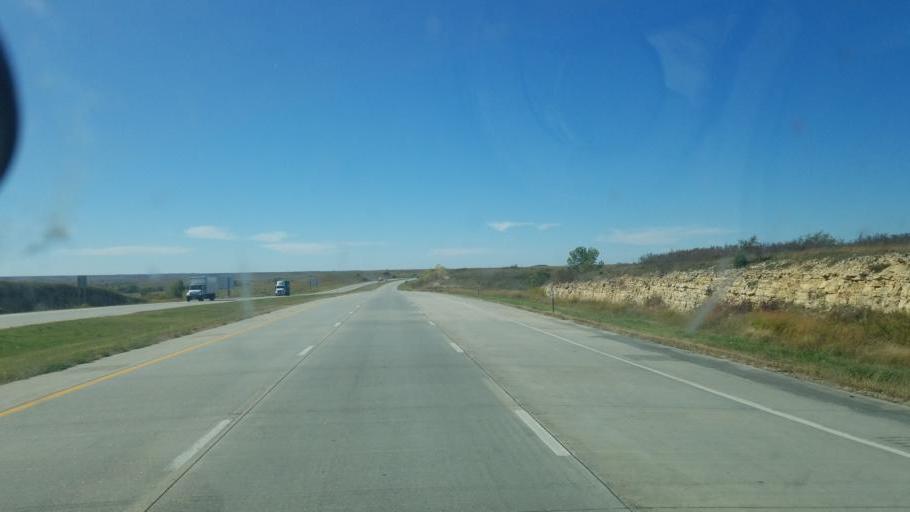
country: US
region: Kansas
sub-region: Riley County
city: Manhattan
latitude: 39.0627
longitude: -96.5413
